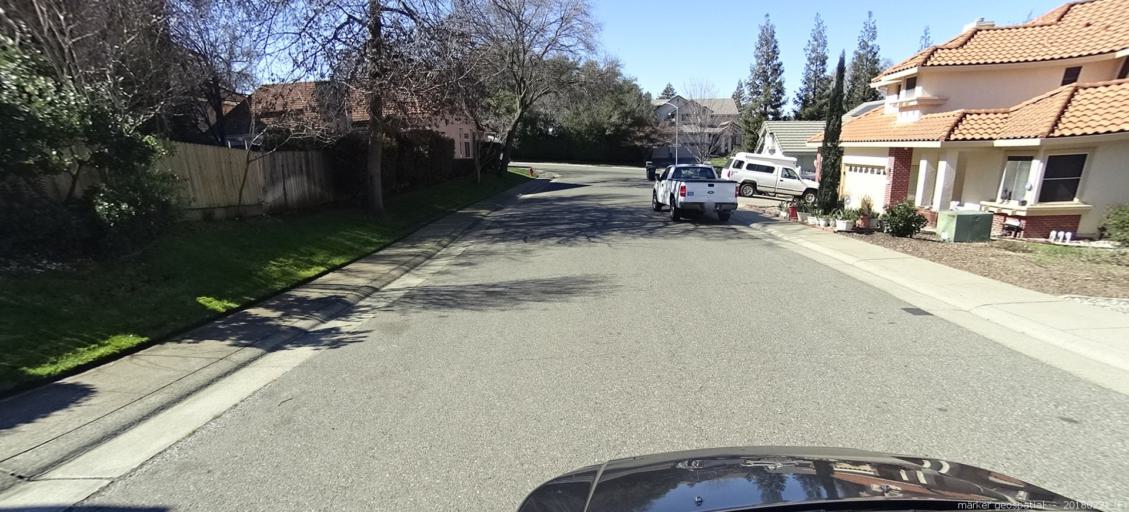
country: US
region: California
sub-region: Sacramento County
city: Orangevale
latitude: 38.6794
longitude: -121.2429
